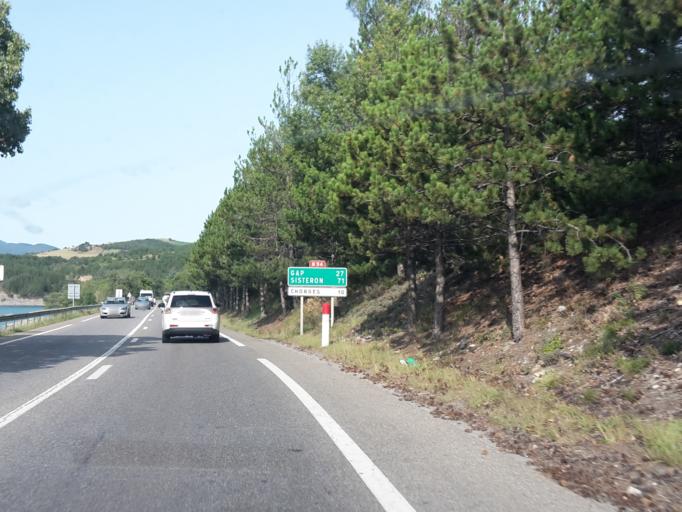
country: FR
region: Provence-Alpes-Cote d'Azur
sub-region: Departement des Hautes-Alpes
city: Embrun
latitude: 44.5356
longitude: 6.3898
